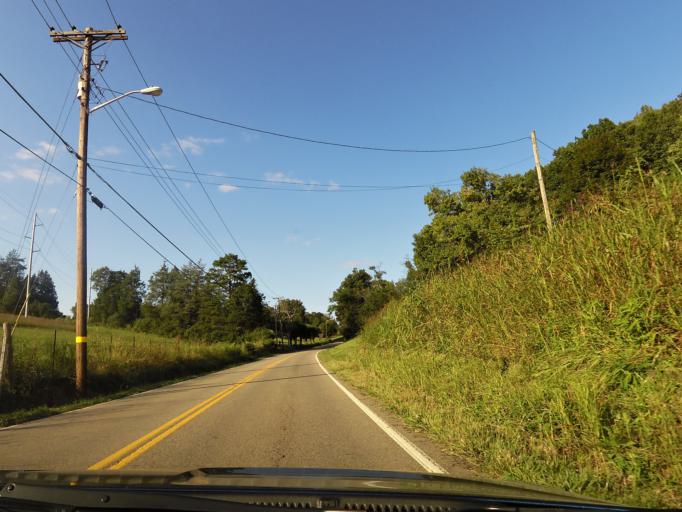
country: US
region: Tennessee
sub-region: Union County
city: Condon
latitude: 36.1836
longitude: -83.8134
